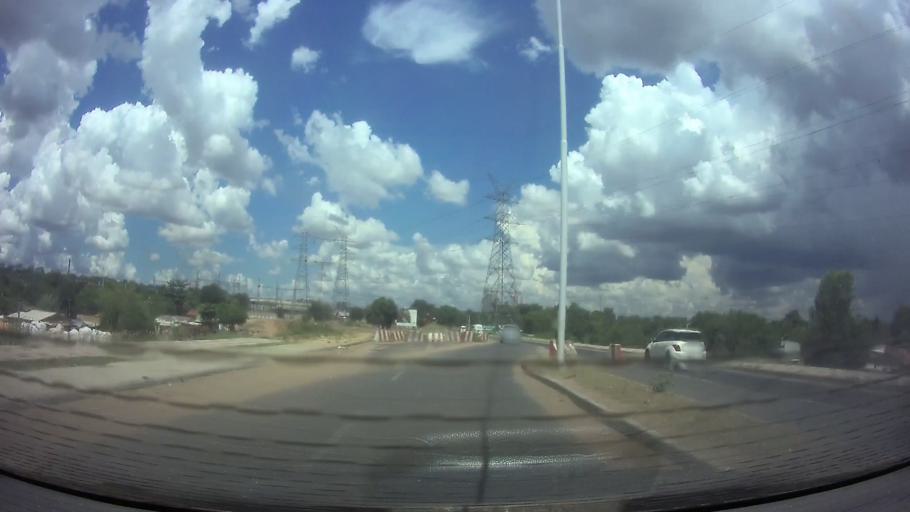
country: PY
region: Asuncion
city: Asuncion
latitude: -25.2469
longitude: -57.5884
